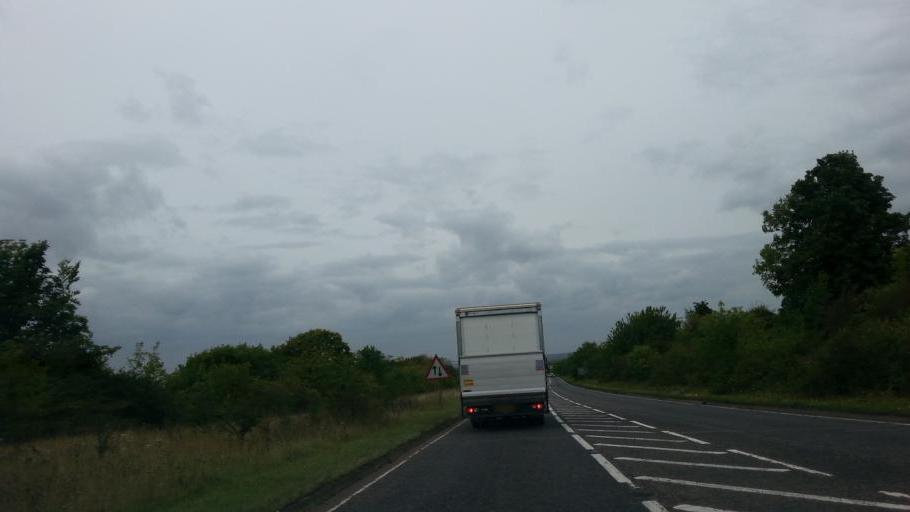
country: GB
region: England
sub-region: Hertfordshire
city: Royston
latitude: 52.0527
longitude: -0.0034
